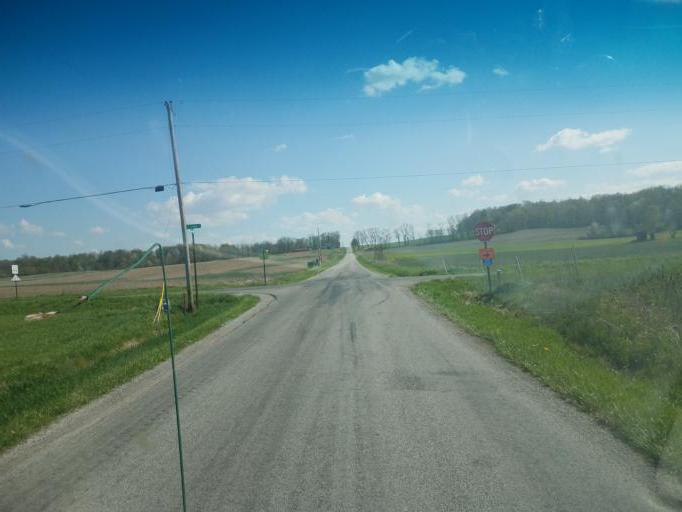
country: US
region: Ohio
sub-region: Medina County
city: Westfield Center
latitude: 40.9861
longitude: -81.9388
